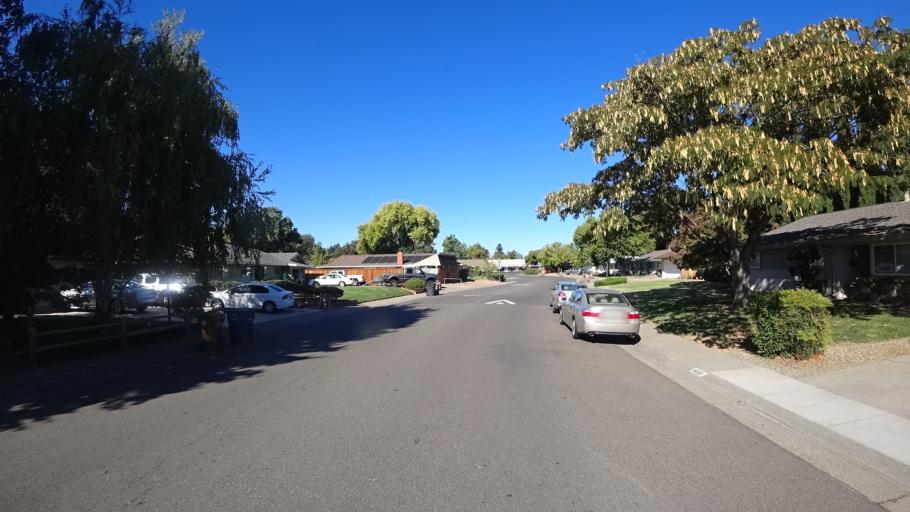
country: US
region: California
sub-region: Sacramento County
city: Elk Grove
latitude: 38.4033
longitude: -121.3698
